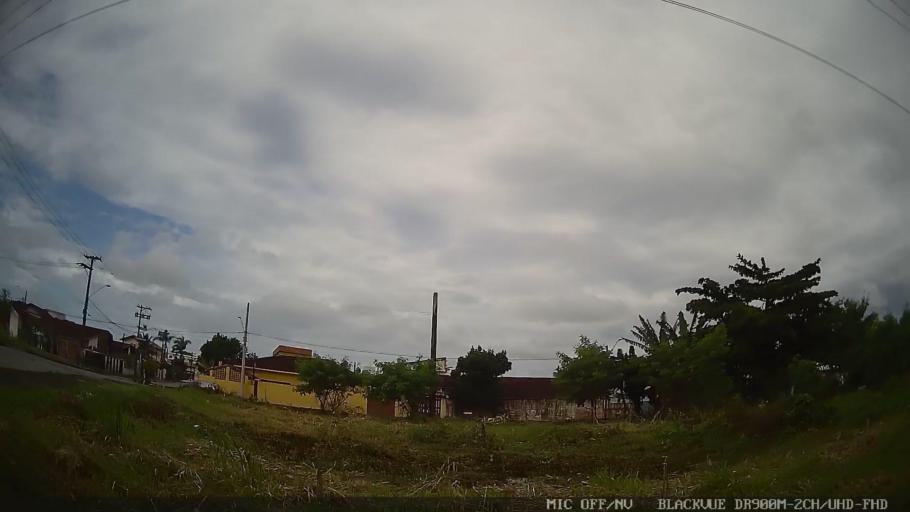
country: BR
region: Sao Paulo
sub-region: Itanhaem
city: Itanhaem
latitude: -24.1753
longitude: -46.7753
